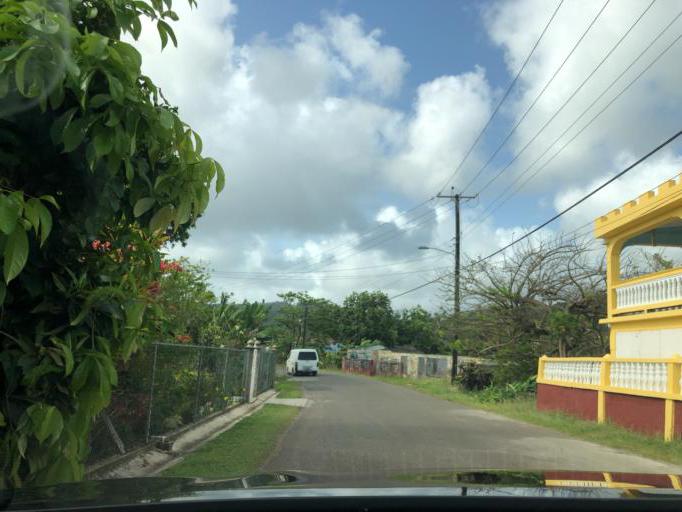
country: LC
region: Castries Quarter
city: Bisee
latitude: 13.9947
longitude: -60.9553
